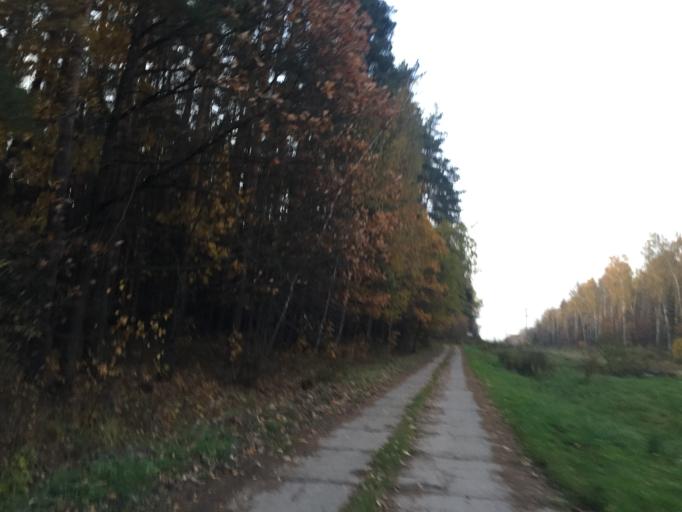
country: RU
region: Moskovskaya
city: Druzhba
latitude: 55.8661
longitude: 37.7676
